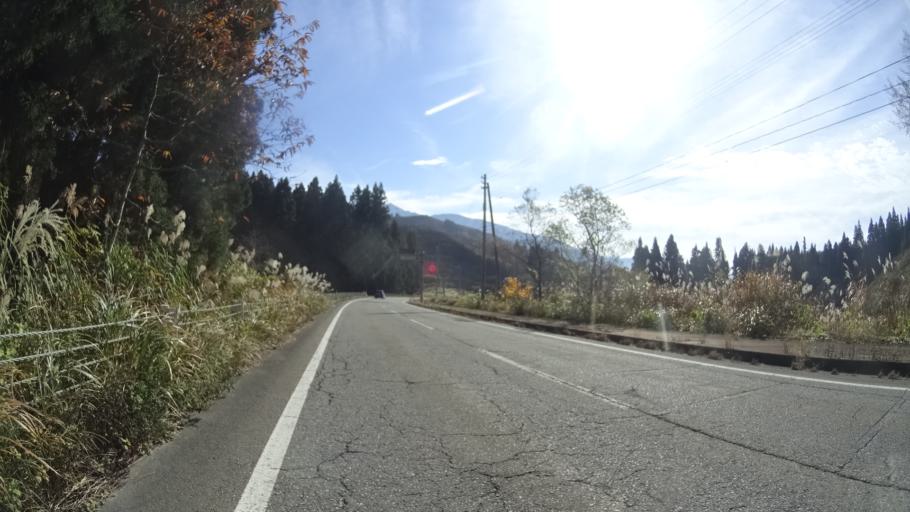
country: JP
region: Niigata
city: Muikamachi
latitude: 37.1901
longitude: 138.9813
